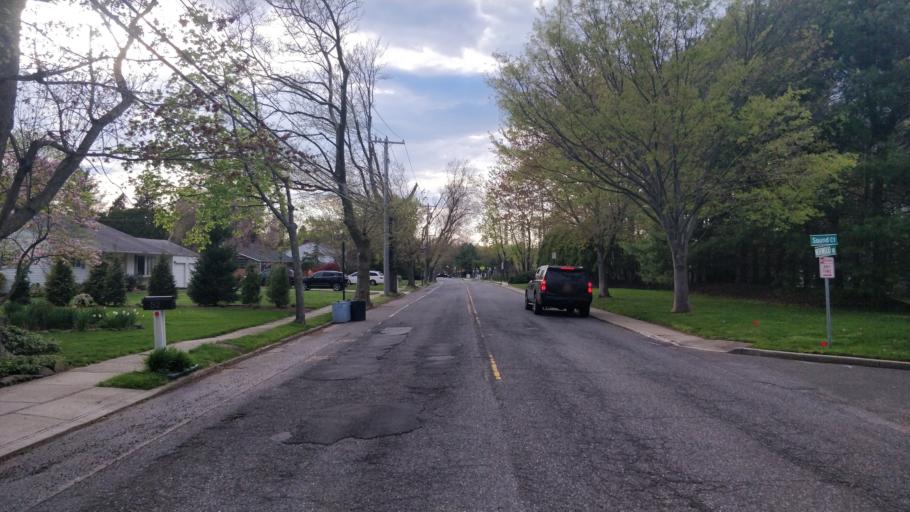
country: US
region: New York
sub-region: Suffolk County
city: Northport
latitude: 40.9112
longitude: -73.3235
